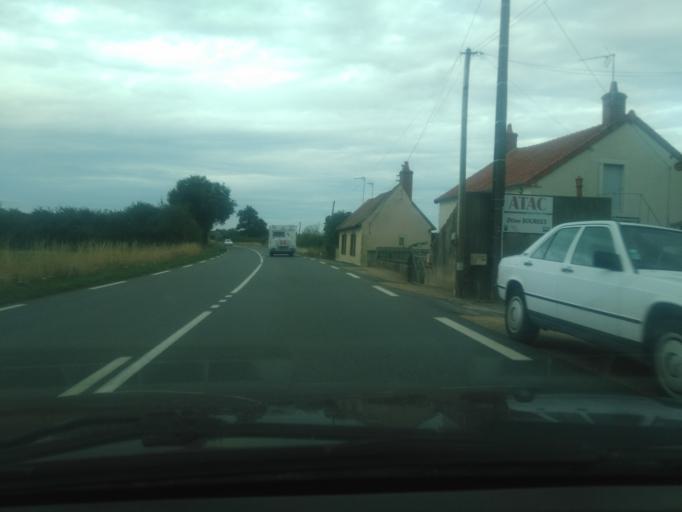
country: FR
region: Centre
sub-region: Departement du Cher
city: Sancoins
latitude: 46.8181
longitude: 2.9146
